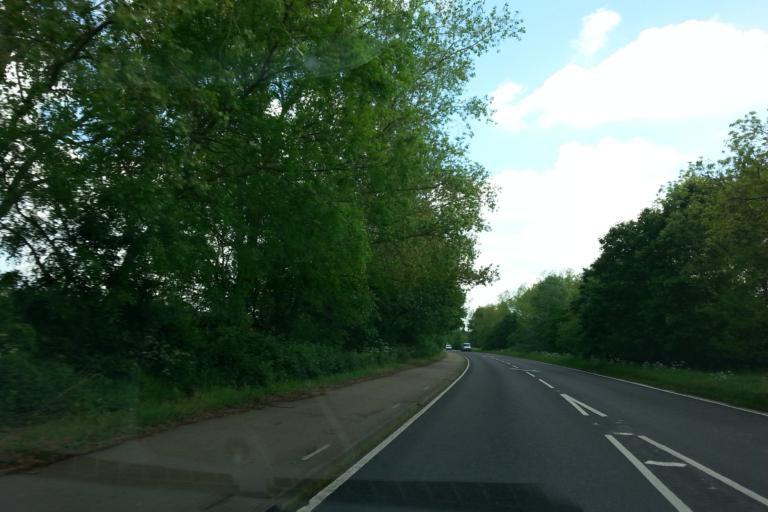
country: GB
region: England
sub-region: Cambridgeshire
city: Yaxley
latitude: 52.5105
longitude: -0.2764
